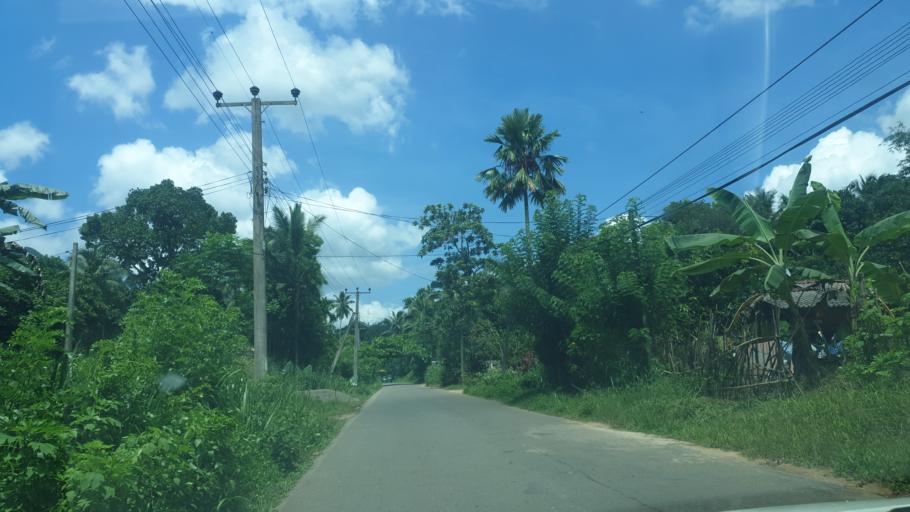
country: LK
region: Sabaragamuwa
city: Ratnapura
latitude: 6.4947
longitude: 80.3954
